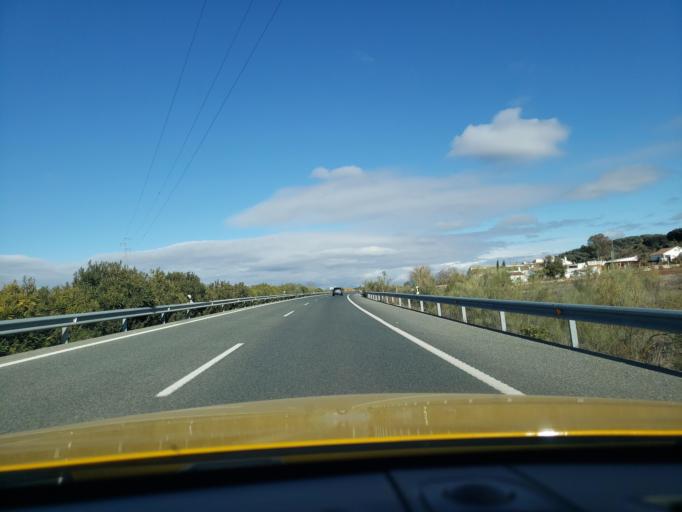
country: ES
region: Andalusia
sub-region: Provincia de Malaga
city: Archidona
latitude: 37.0982
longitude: -4.3153
